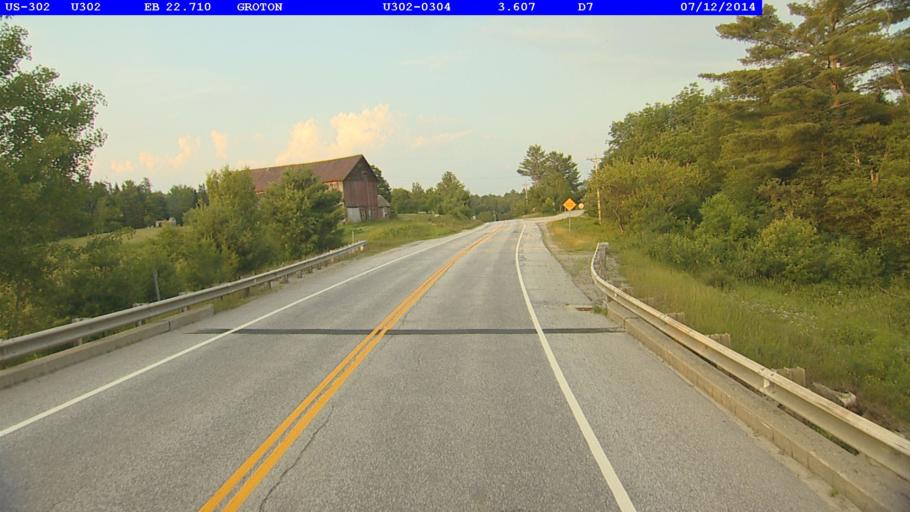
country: US
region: New Hampshire
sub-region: Grafton County
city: Woodsville
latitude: 44.2167
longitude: -72.2476
